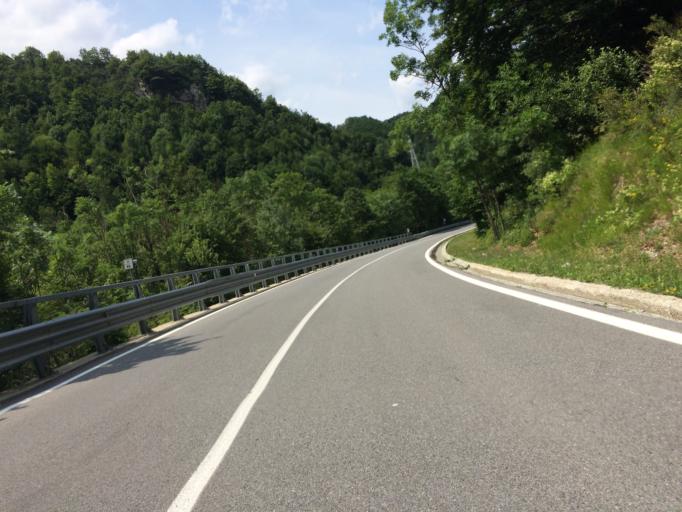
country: IT
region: Piedmont
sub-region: Provincia di Cuneo
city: Limone Piemonte
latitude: 44.2255
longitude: 7.5633
